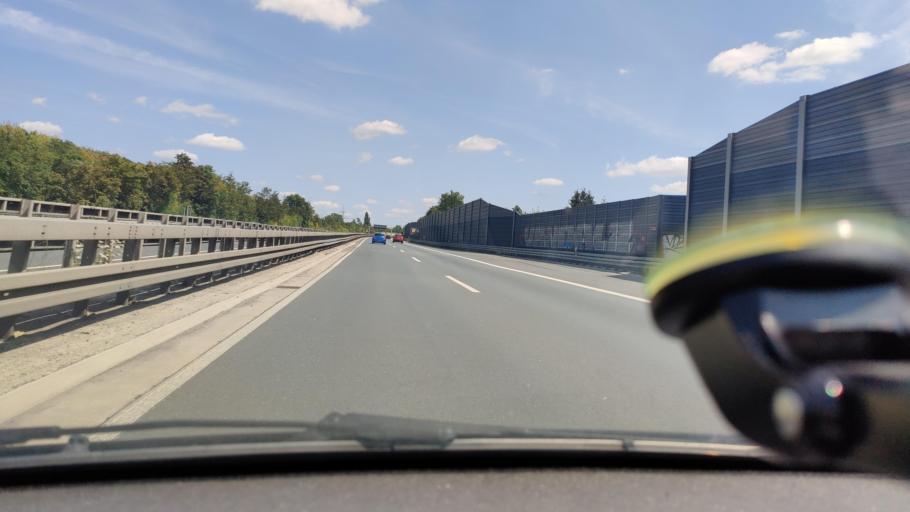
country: DE
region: North Rhine-Westphalia
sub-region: Regierungsbezirk Dusseldorf
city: Essen
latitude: 51.5110
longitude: 7.0185
